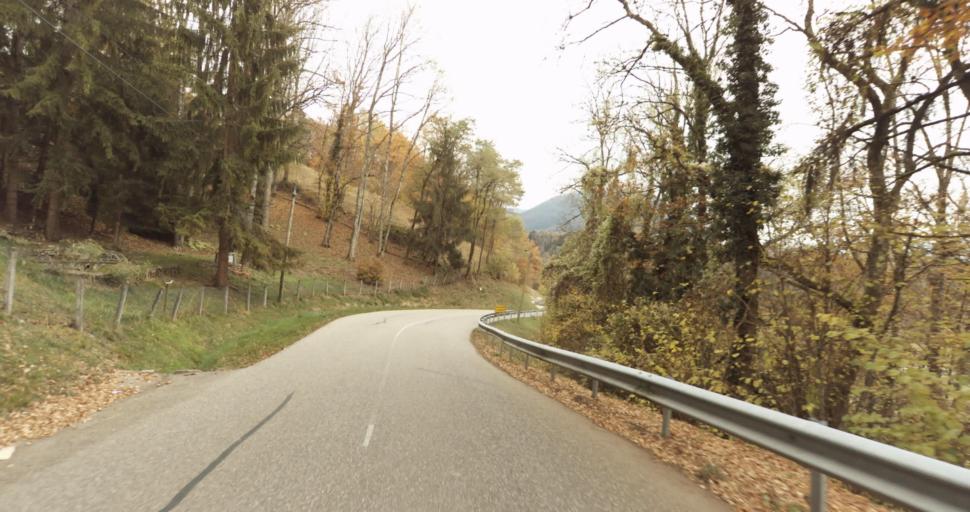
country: FR
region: Rhone-Alpes
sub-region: Departement de la Haute-Savoie
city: Villaz
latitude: 45.9426
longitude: 6.1691
